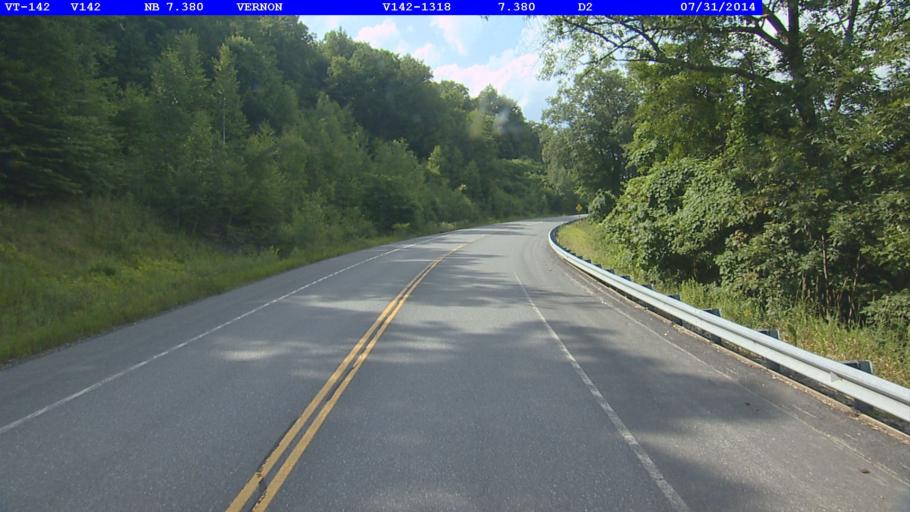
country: US
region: Vermont
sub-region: Windham County
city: Brattleboro
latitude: 42.8069
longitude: -72.5424
